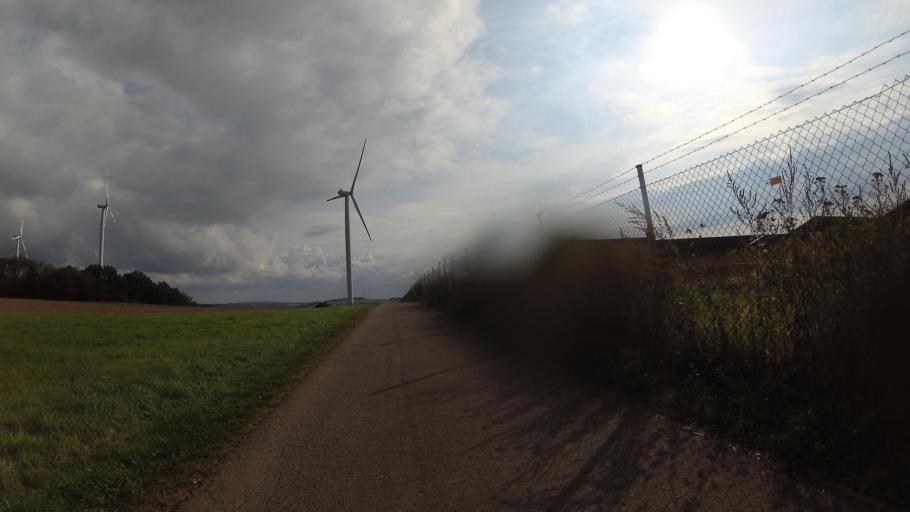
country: DE
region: Saarland
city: Freisen
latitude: 49.5069
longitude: 7.2455
